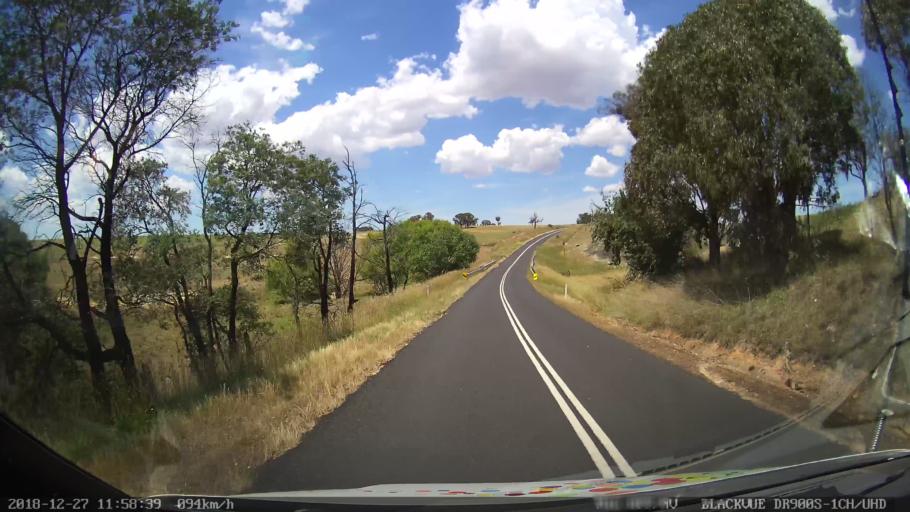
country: AU
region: New South Wales
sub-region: Blayney
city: Blayney
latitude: -33.7268
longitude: 149.3832
